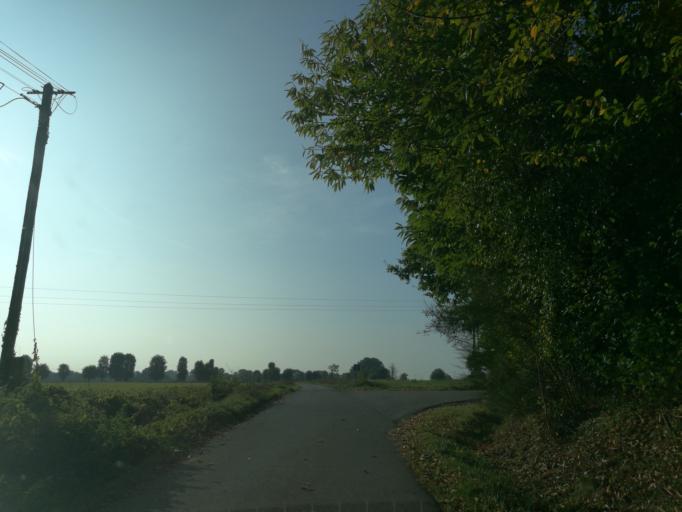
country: FR
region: Brittany
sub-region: Departement d'Ille-et-Vilaine
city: Pleumeleuc
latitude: 48.1646
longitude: -1.9118
